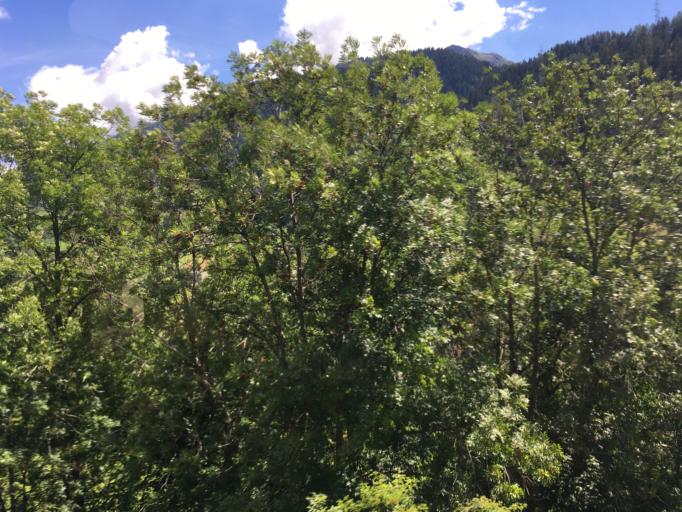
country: CH
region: Valais
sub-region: Goms District
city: Fiesch
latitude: 46.3889
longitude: 8.1211
